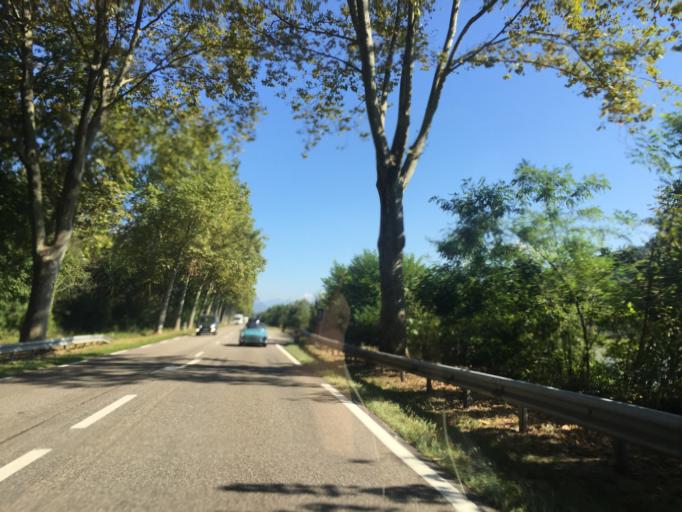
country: FR
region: Rhone-Alpes
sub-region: Departement de la Savoie
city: Cruet
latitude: 45.5241
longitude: 6.1084
